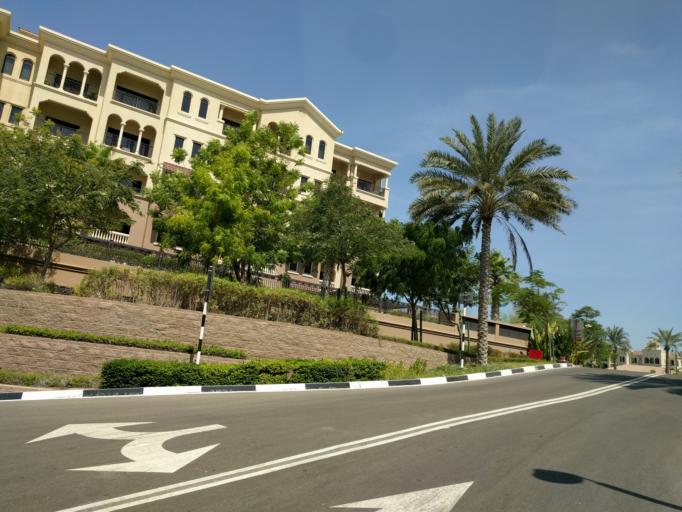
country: AE
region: Abu Dhabi
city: Abu Dhabi
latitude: 24.5496
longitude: 54.4536
